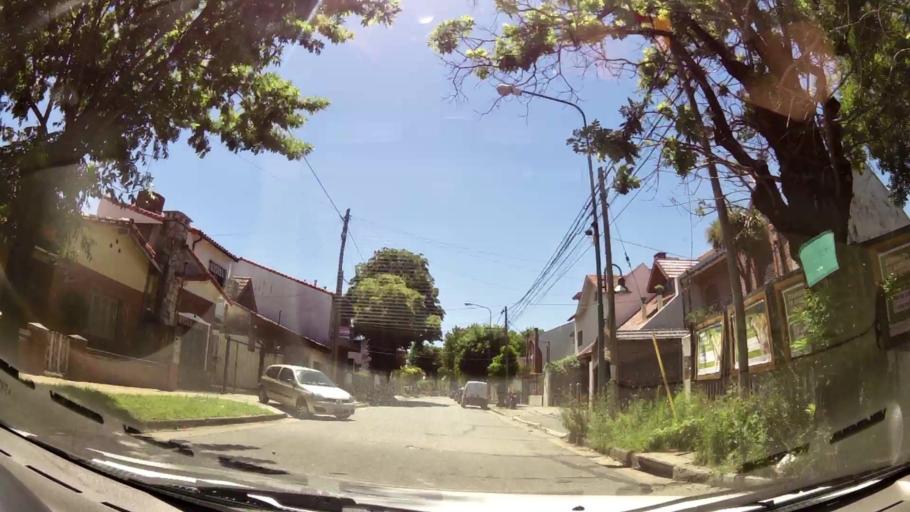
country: AR
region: Buenos Aires
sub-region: Partido de Vicente Lopez
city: Olivos
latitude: -34.5047
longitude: -58.5041
